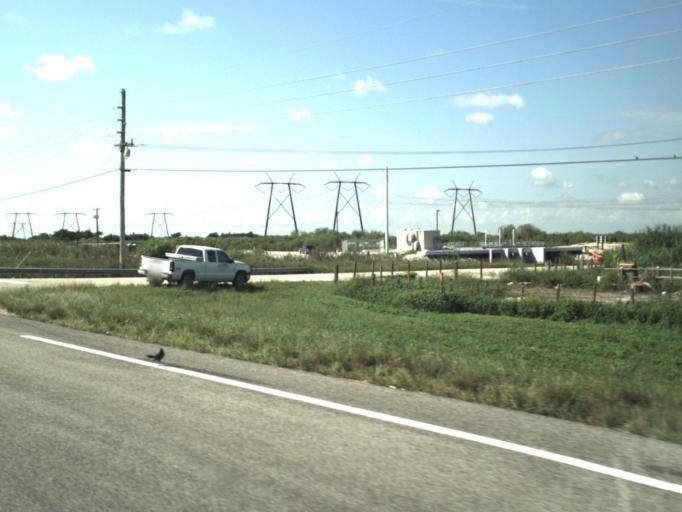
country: US
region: Florida
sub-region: Broward County
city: Weston
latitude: 26.3364
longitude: -80.5393
